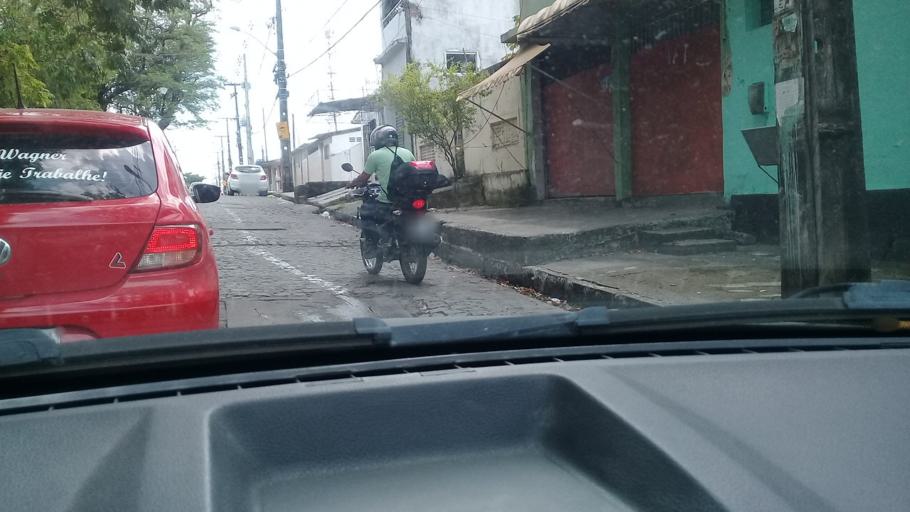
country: BR
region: Pernambuco
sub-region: Jaboatao Dos Guararapes
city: Jaboatao dos Guararapes
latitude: -8.1199
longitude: -34.9484
